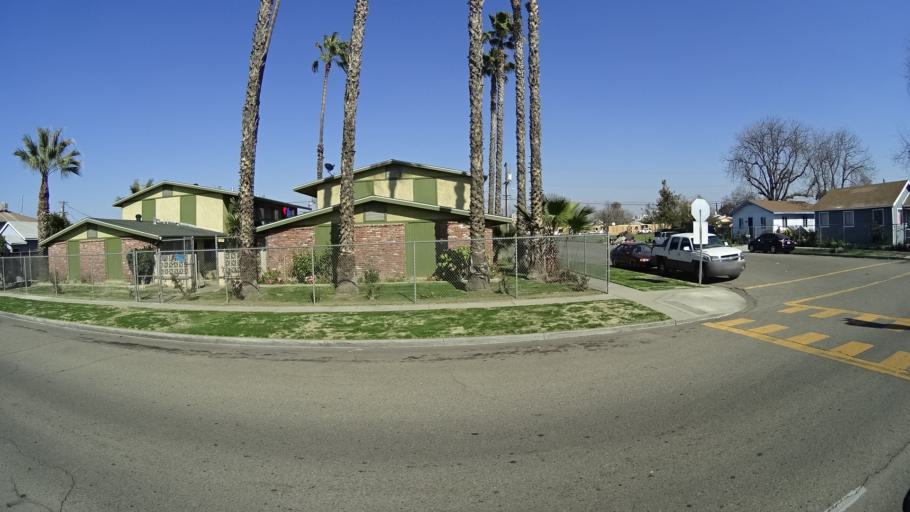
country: US
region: California
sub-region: Fresno County
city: Fresno
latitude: 36.7329
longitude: -119.8068
